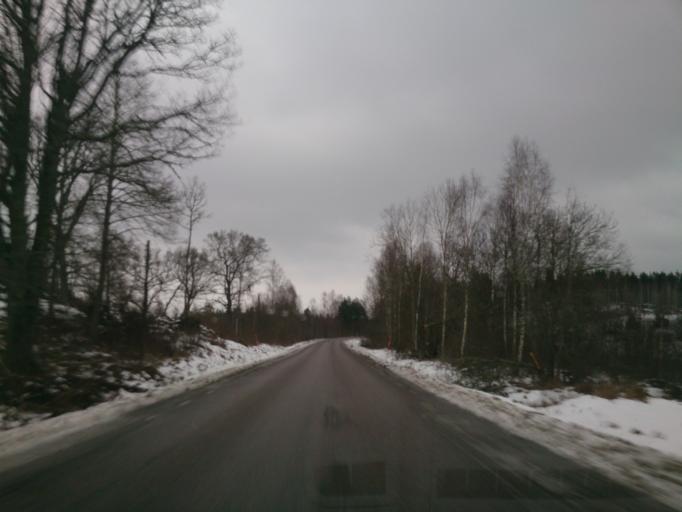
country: SE
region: OEstergoetland
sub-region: Atvidabergs Kommun
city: Atvidaberg
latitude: 58.2272
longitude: 15.9937
